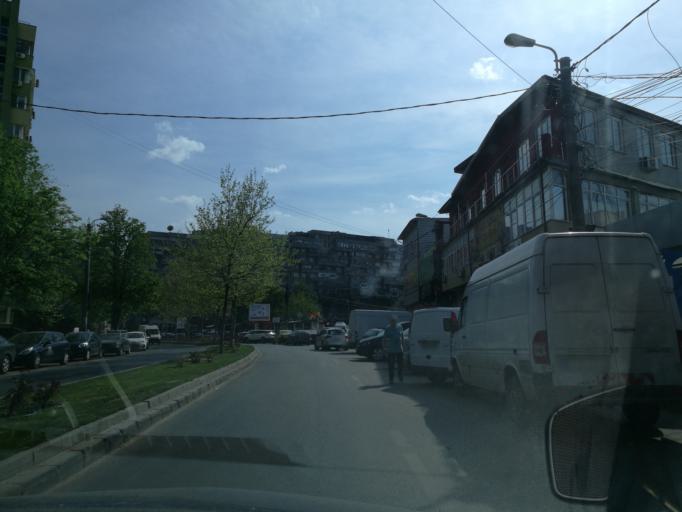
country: RO
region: Ilfov
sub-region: Comuna Chiajna
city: Rosu
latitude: 44.4353
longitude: 26.0209
